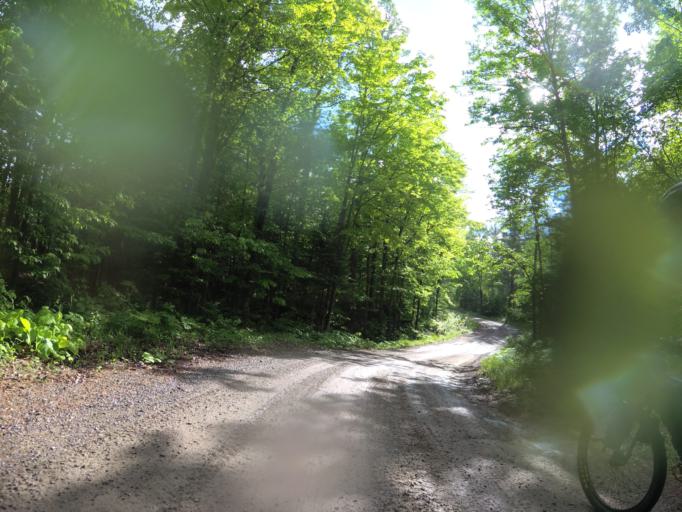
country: CA
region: Ontario
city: Renfrew
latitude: 45.1785
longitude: -76.9241
